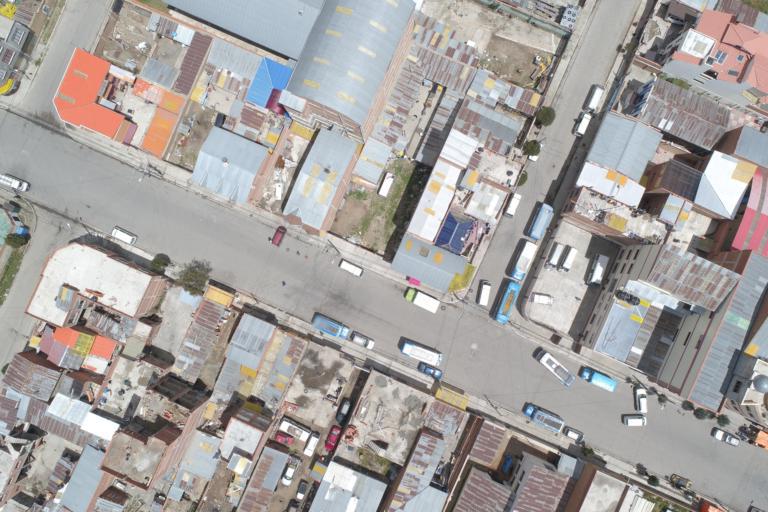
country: BO
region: La Paz
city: La Paz
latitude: -16.5313
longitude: -68.1489
